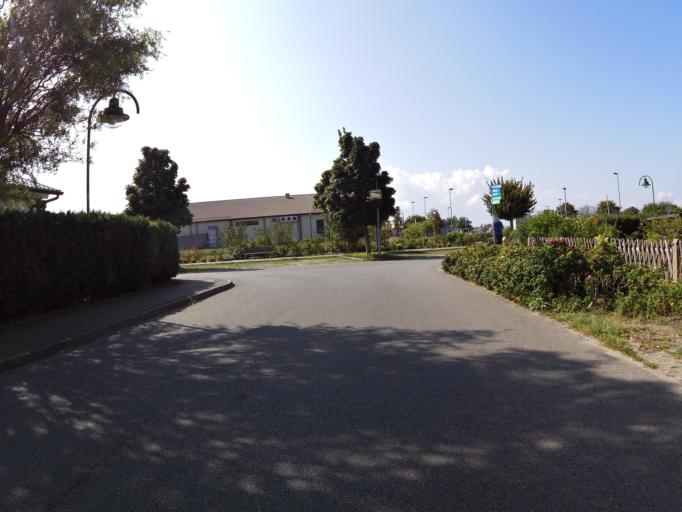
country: DE
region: Mecklenburg-Vorpommern
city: Loddin
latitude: 54.0154
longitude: 14.0484
